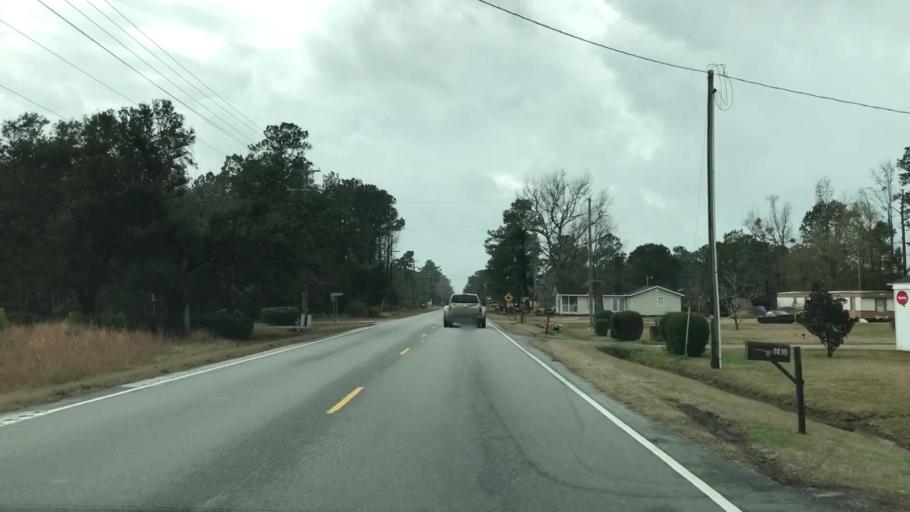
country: US
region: South Carolina
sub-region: Horry County
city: Socastee
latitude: 33.6933
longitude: -79.1155
